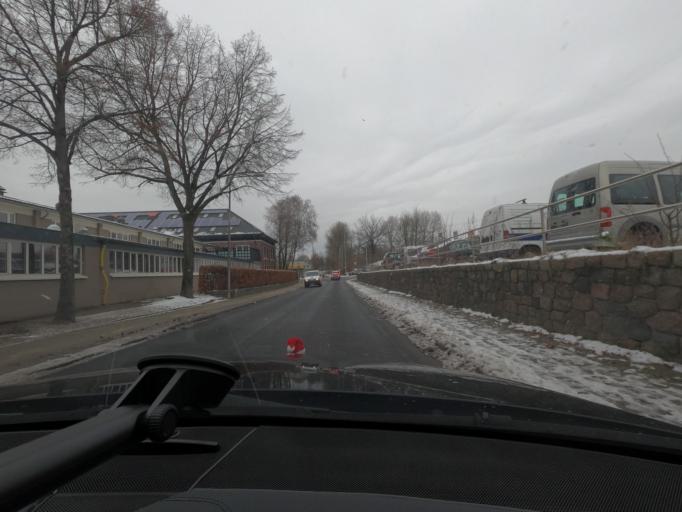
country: DE
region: Schleswig-Holstein
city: Flensburg
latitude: 54.7708
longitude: 9.4263
